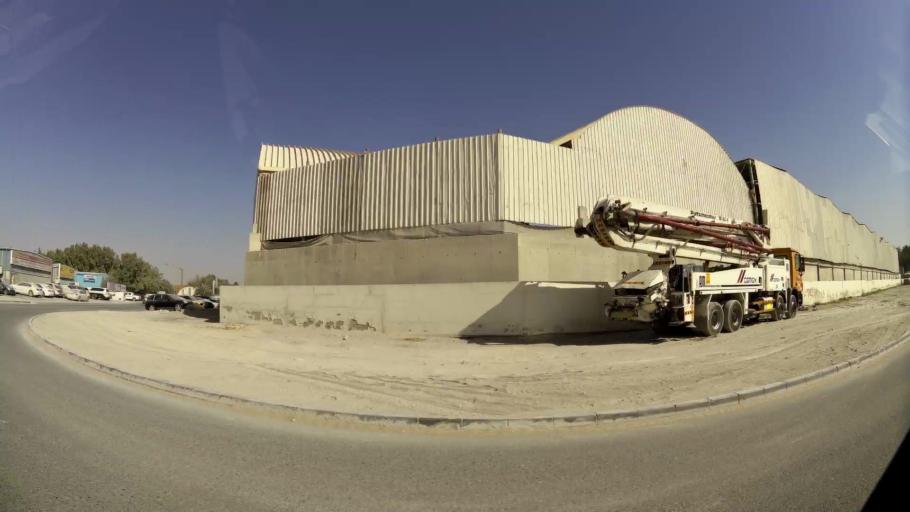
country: AE
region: Dubai
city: Dubai
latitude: 25.1357
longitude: 55.2205
